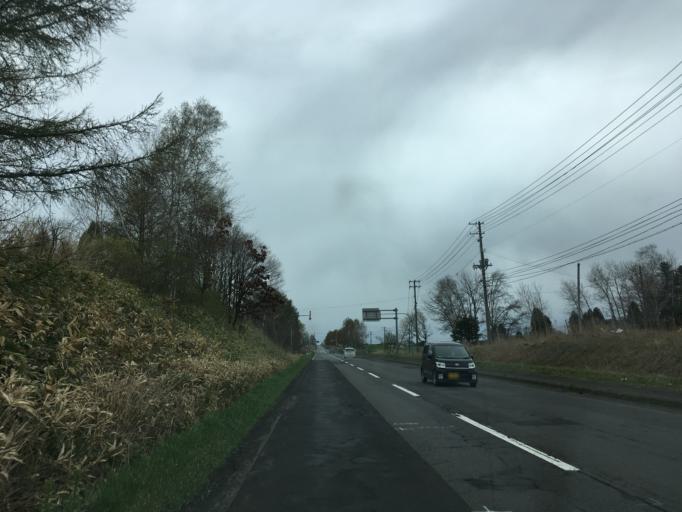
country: JP
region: Hokkaido
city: Chitose
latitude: 42.9122
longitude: 141.8109
